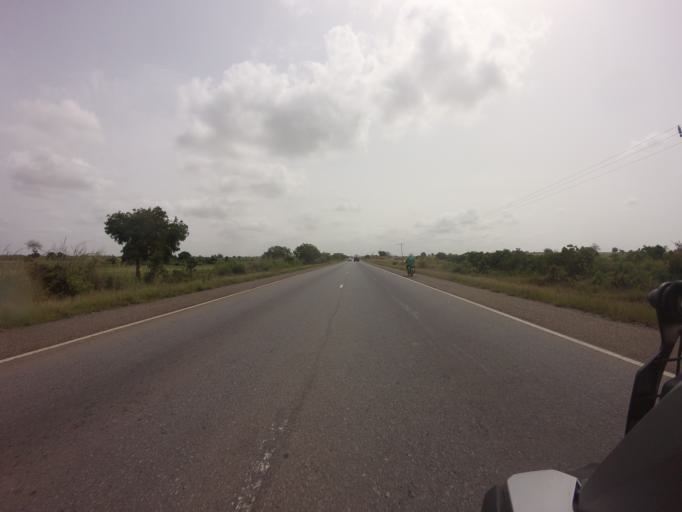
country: GH
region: Volta
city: Anloga
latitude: 5.8863
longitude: 0.4465
